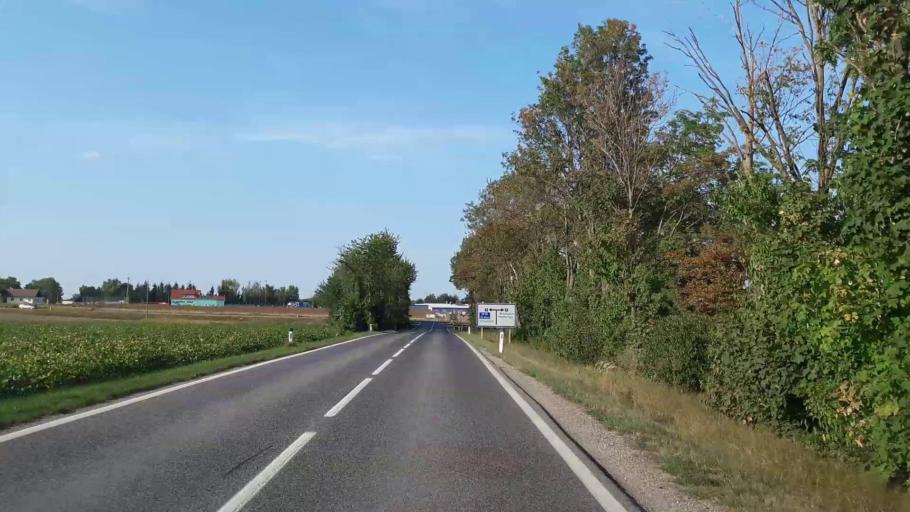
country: AT
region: Lower Austria
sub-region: Politischer Bezirk Ganserndorf
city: Mannsdorf an der Donau
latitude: 48.1095
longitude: 16.6719
